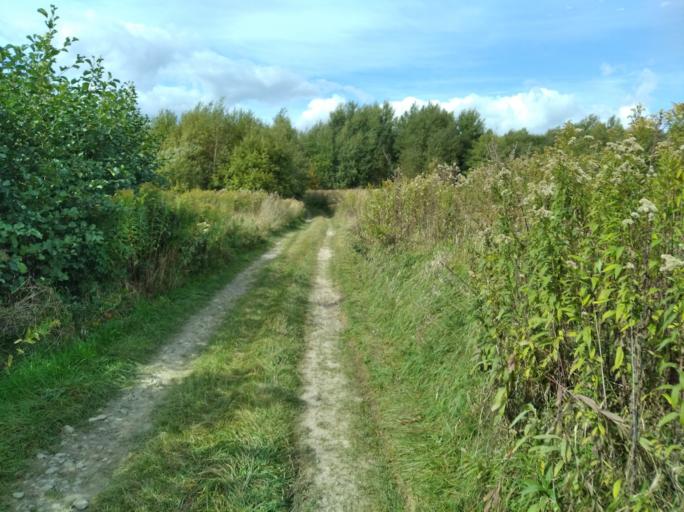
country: PL
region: Subcarpathian Voivodeship
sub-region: Powiat strzyzowski
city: Jawornik
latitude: 49.8457
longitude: 21.8610
